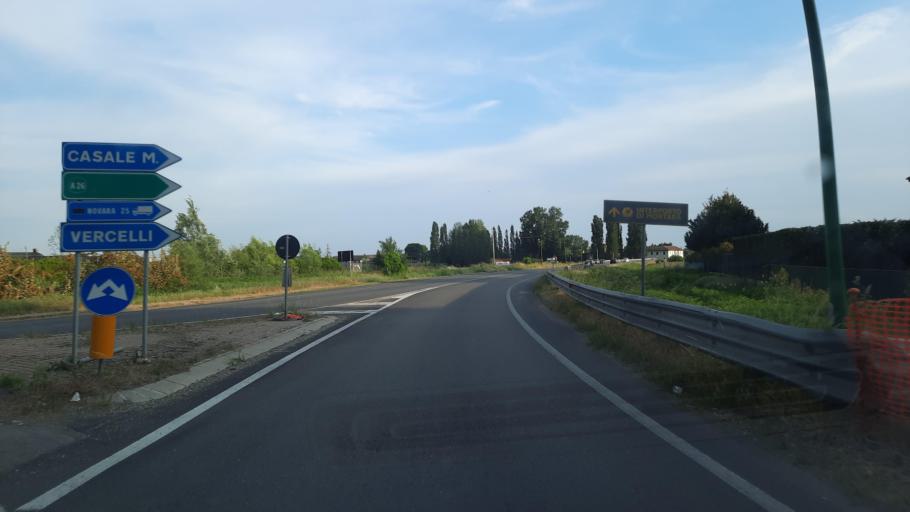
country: IT
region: Lombardy
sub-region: Provincia di Pavia
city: Mortara
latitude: 45.2500
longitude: 8.7532
